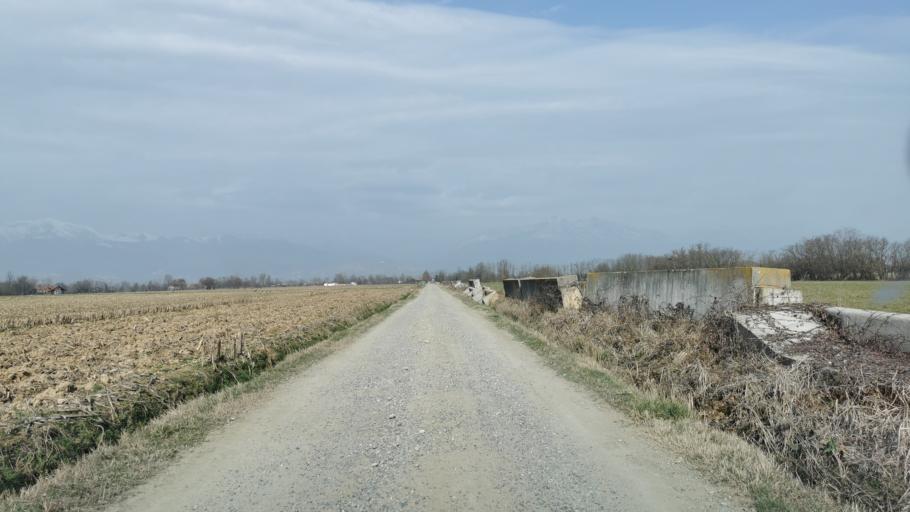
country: IT
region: Piedmont
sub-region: Provincia di Torino
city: Rivarossa
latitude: 45.2755
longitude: 7.7015
